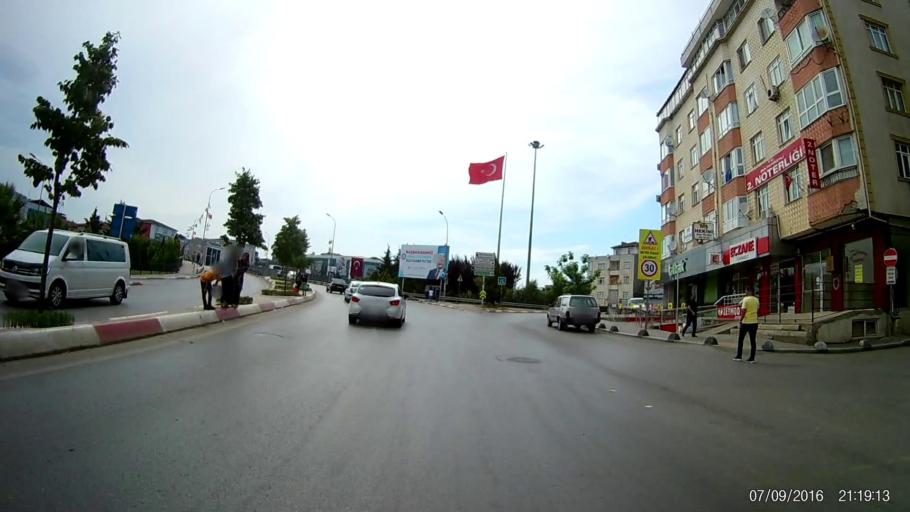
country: TR
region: Istanbul
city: Sultanbeyli
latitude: 40.9663
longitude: 29.2745
